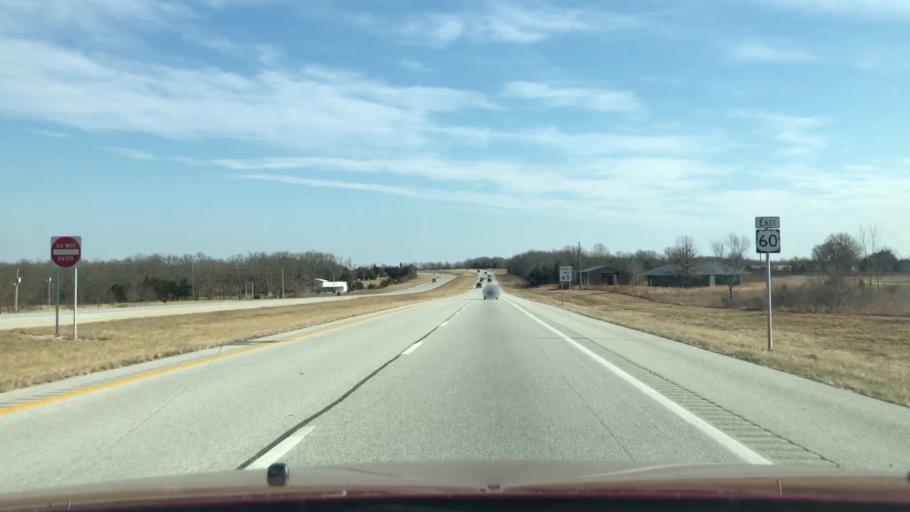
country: US
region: Missouri
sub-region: Webster County
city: Seymour
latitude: 37.1637
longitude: -92.8824
